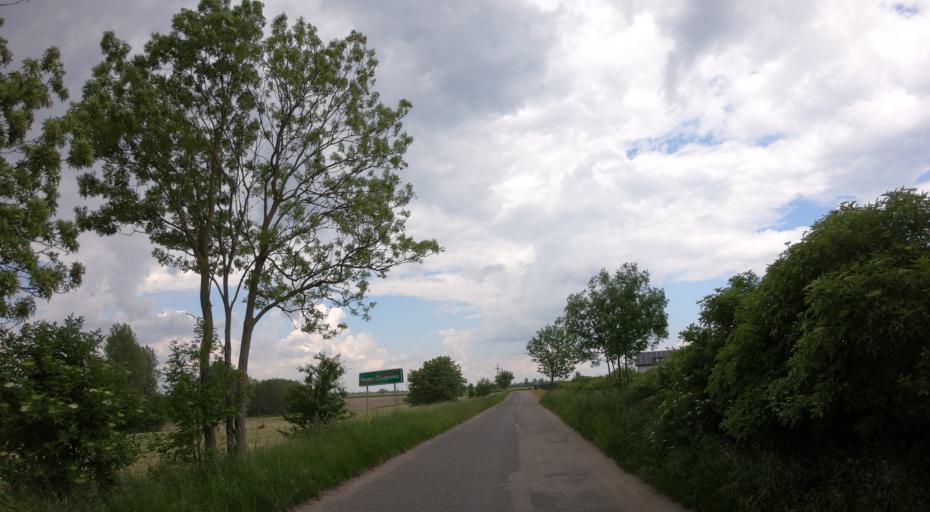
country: PL
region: West Pomeranian Voivodeship
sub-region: Powiat pyrzycki
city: Kozielice
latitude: 53.1540
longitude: 14.7928
